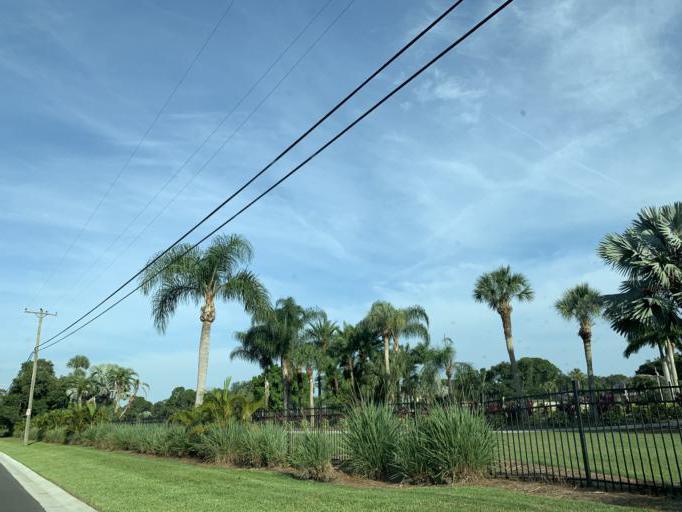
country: US
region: Florida
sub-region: Pinellas County
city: Lealman
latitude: 27.8031
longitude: -82.6300
